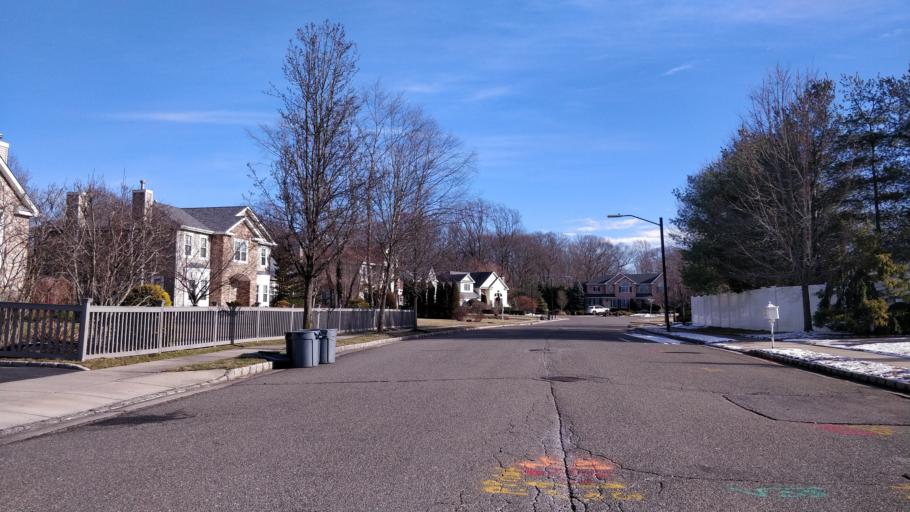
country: US
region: New York
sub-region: Nassau County
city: Oyster Bay
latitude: 40.8555
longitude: -73.5228
